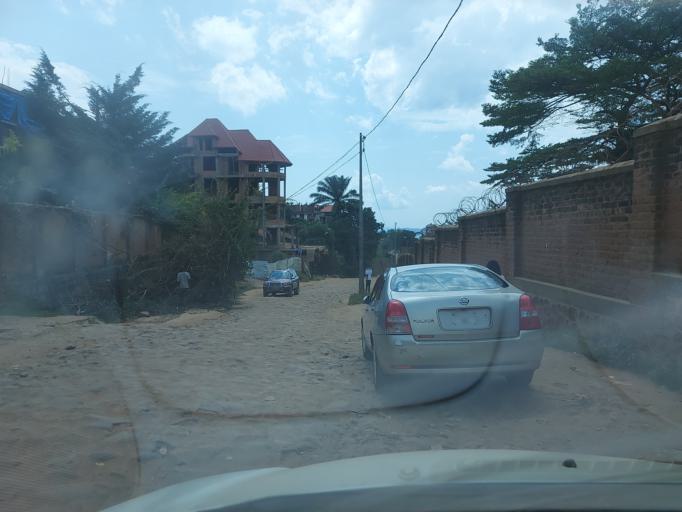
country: CD
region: South Kivu
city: Bukavu
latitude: -2.5047
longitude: 28.8613
